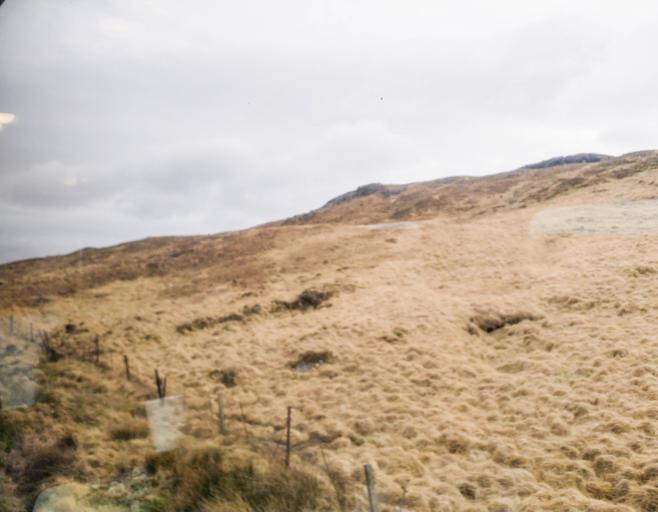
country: GB
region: Scotland
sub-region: Highland
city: Spean Bridge
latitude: 56.5895
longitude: -4.6535
